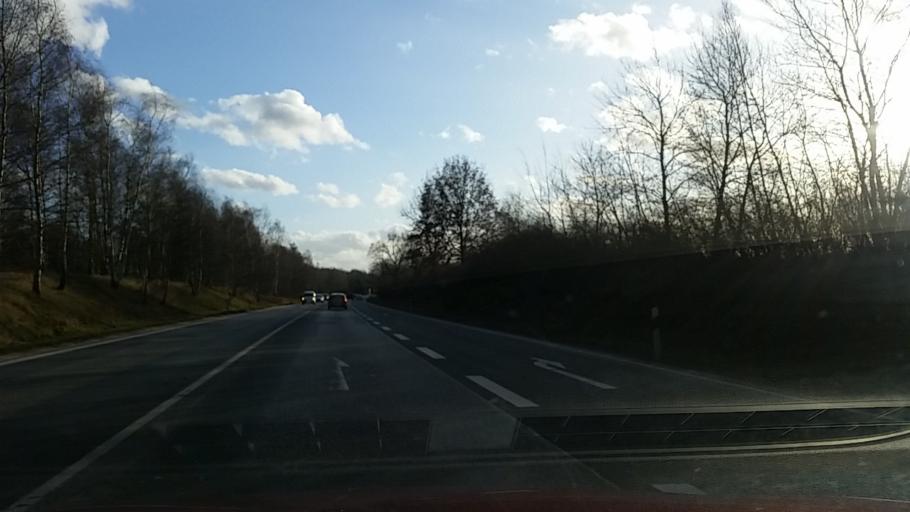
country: DE
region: Schleswig-Holstein
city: Glinde
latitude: 53.5538
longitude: 10.2337
